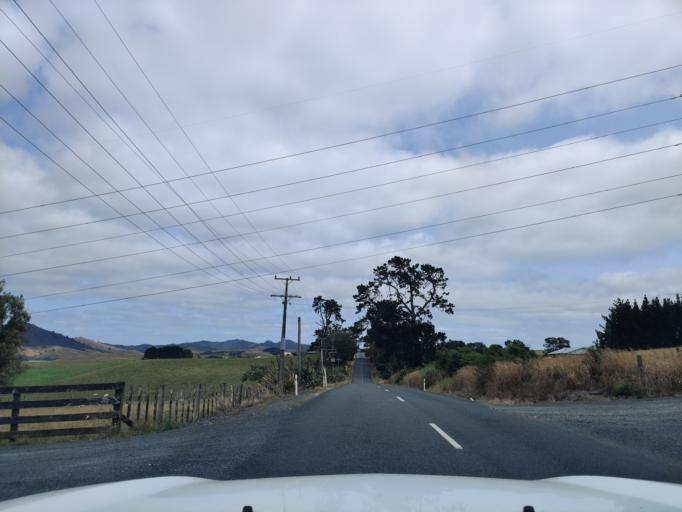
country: NZ
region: Waikato
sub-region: Waikato District
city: Te Kauwhata
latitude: -37.5160
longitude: 175.1763
